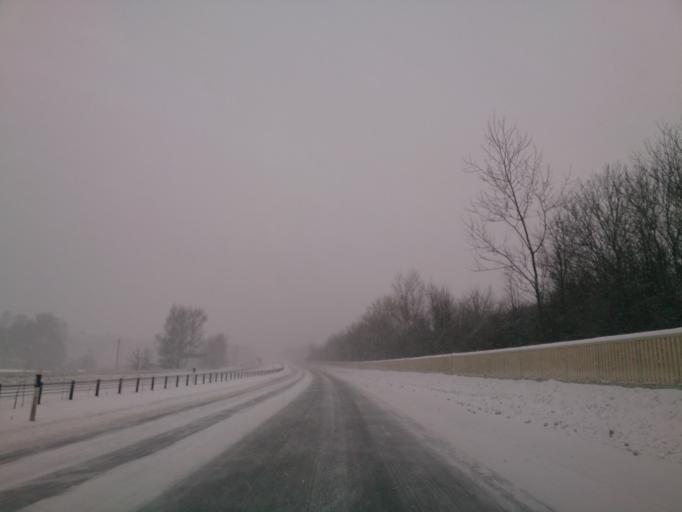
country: SE
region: Soedermanland
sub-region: Nykopings Kommun
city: Nykoping
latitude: 58.7538
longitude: 16.9808
